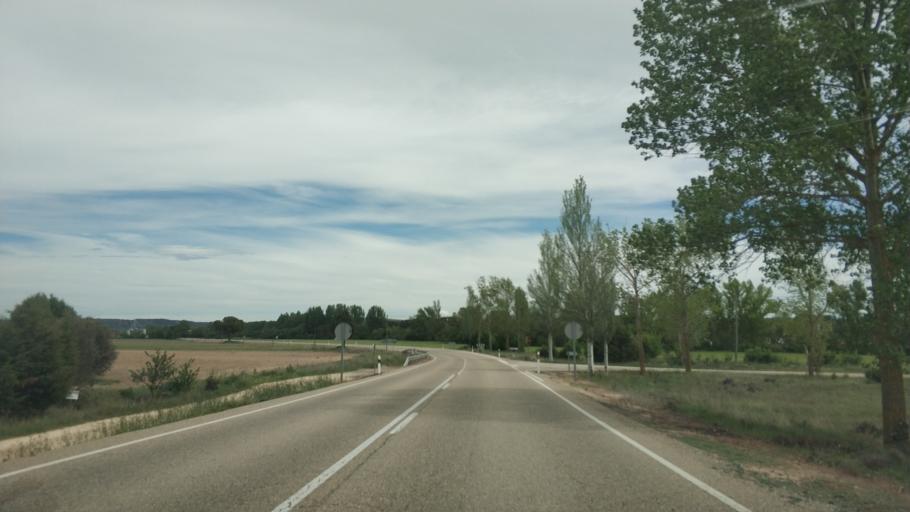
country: ES
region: Castille and Leon
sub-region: Provincia de Soria
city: Bayubas de Abajo
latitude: 41.5021
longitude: -2.8876
